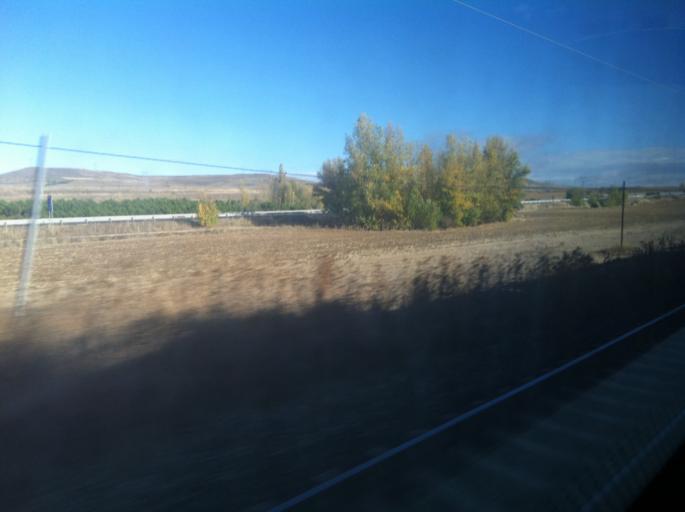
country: ES
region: Castille and Leon
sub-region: Provincia de Burgos
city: Villaldemiro
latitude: 42.2439
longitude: -3.9674
